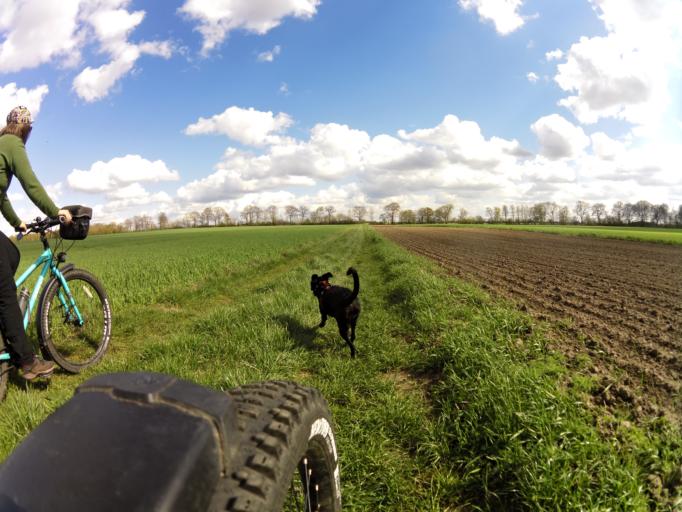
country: PL
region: West Pomeranian Voivodeship
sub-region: Powiat gryficki
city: Ploty
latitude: 53.8327
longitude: 15.2560
